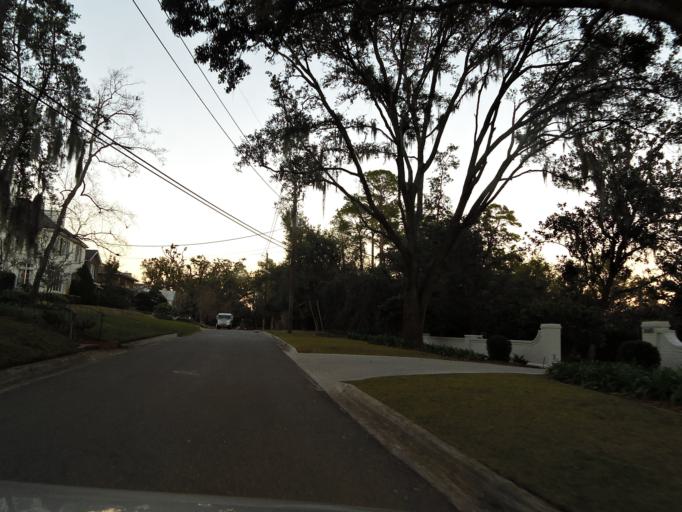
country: US
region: Florida
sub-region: Duval County
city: Jacksonville
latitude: 30.2928
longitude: -81.7040
